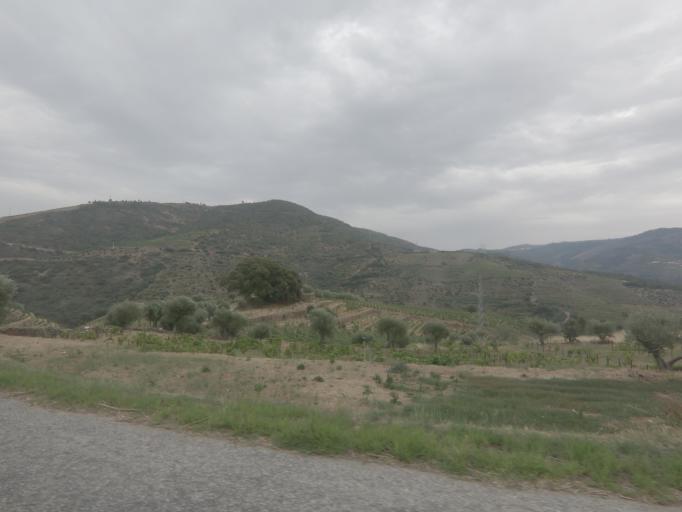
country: PT
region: Viseu
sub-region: Armamar
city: Armamar
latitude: 41.1470
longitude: -7.6445
